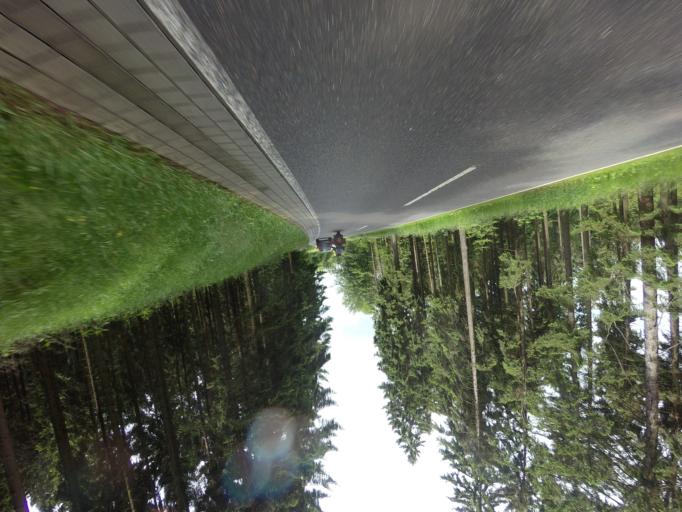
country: DE
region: Rheinland-Pfalz
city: Kaltenborn
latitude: 50.3911
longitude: 7.0127
